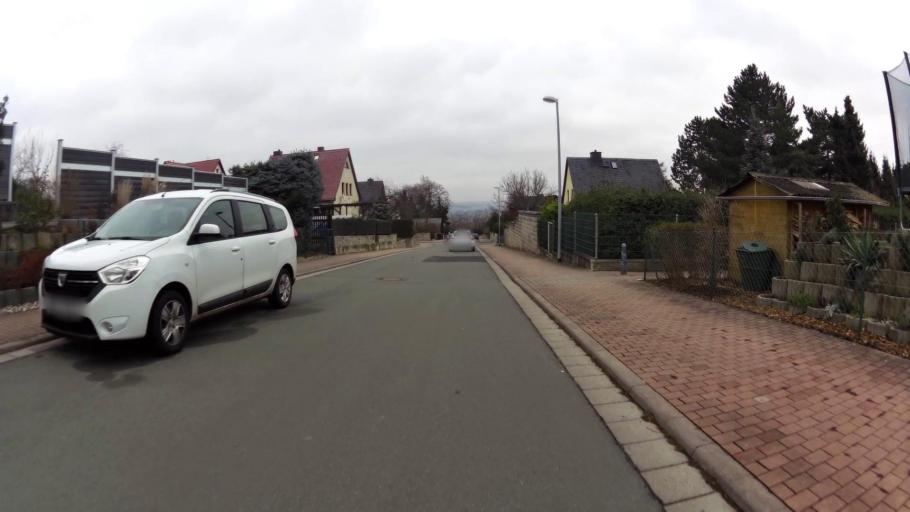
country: DE
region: Thuringia
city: Weimar
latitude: 50.9641
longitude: 11.3256
